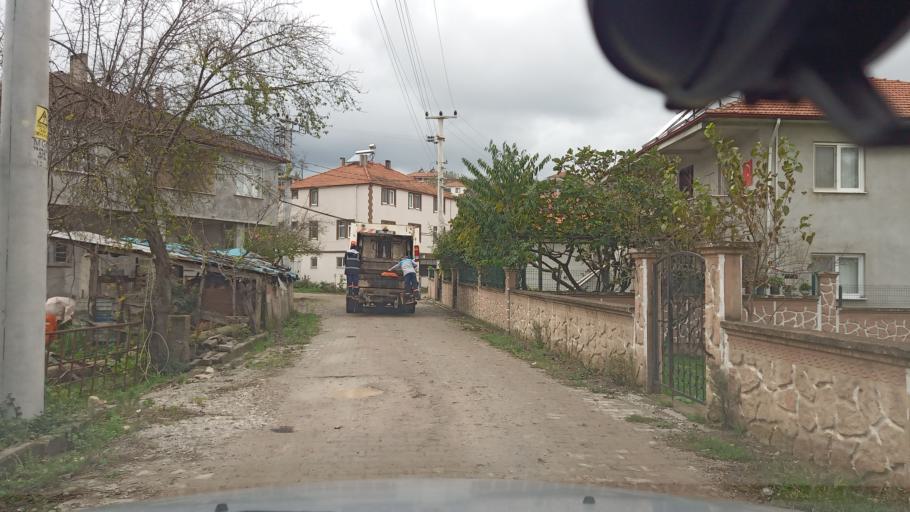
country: TR
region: Sakarya
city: Karasu
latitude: 41.0932
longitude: 30.5834
